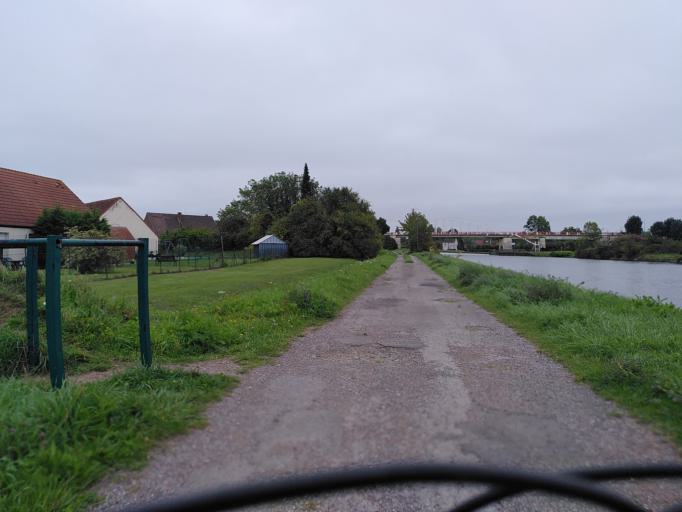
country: FR
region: Nord-Pas-de-Calais
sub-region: Departement du Pas-de-Calais
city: Isbergues
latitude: 50.6312
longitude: 2.4554
